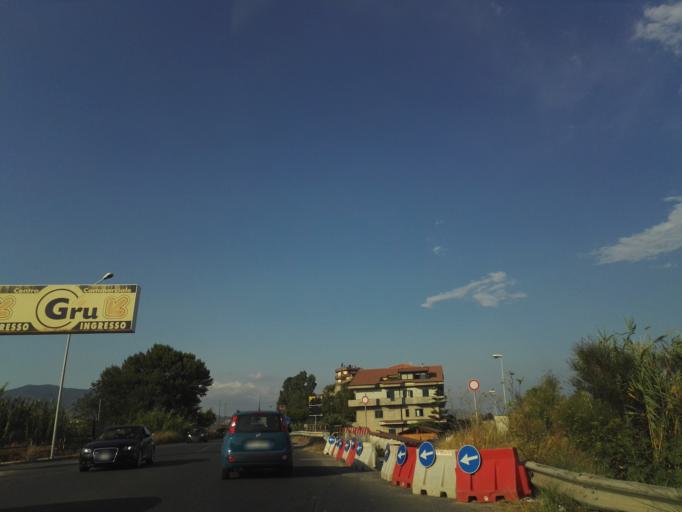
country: IT
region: Calabria
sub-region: Provincia di Reggio Calabria
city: Marina di Gioiosa Ionica
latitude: 38.2908
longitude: 16.3185
